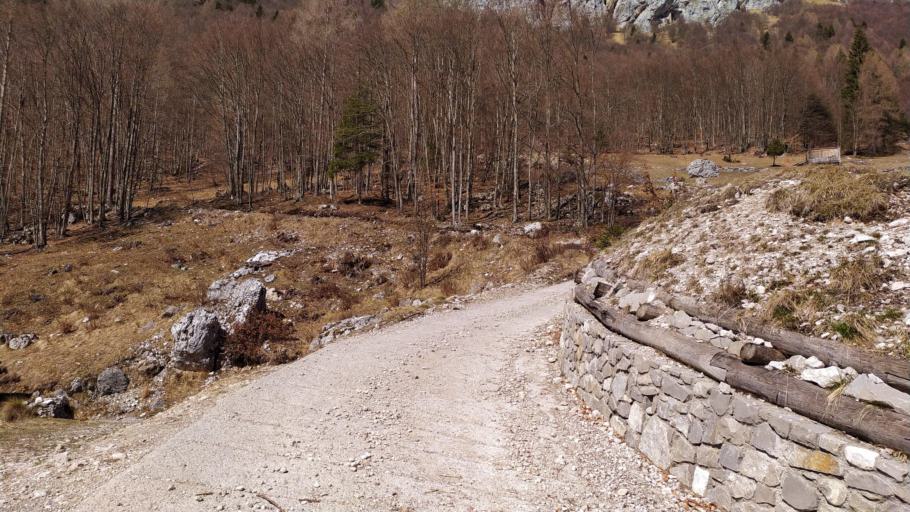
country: IT
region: Friuli Venezia Giulia
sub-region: Provincia di Pordenone
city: Erto
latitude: 46.2944
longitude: 12.3684
